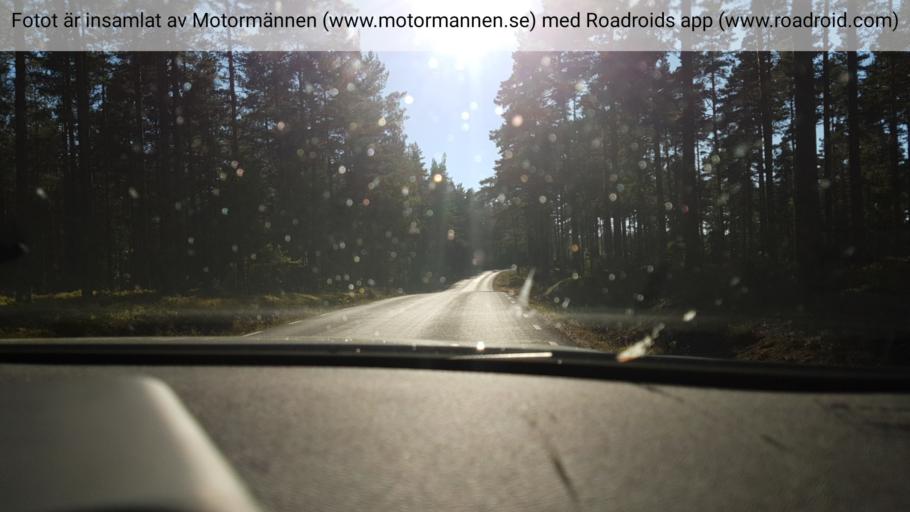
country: SE
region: Vaestra Goetaland
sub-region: Tidaholms Kommun
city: Tidaholm
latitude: 58.0998
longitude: 14.0922
